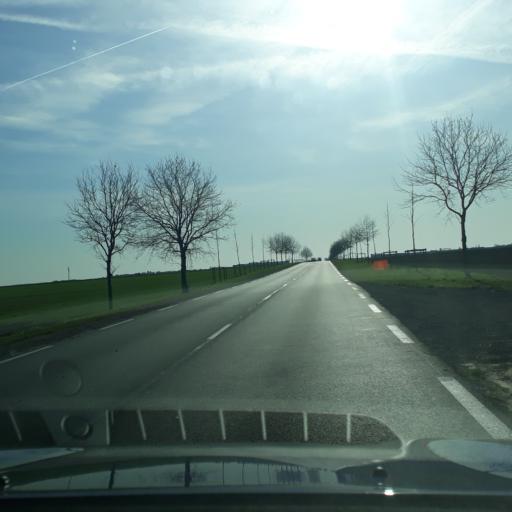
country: FR
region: Ile-de-France
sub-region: Departement de l'Essonne
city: Etampes
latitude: 48.4448
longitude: 2.1189
